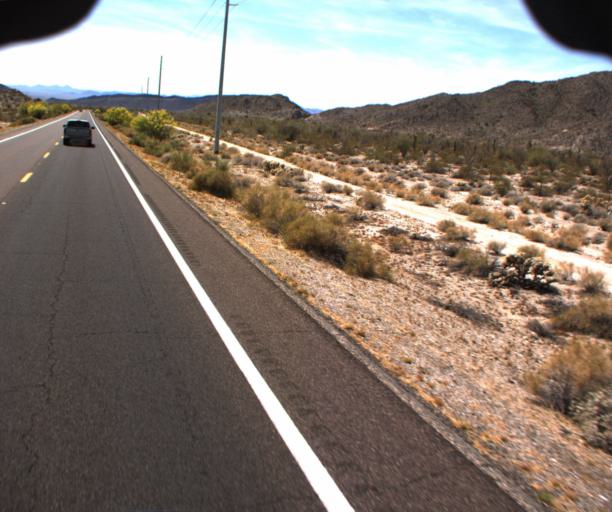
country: US
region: Arizona
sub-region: La Paz County
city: Salome
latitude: 33.7354
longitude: -113.6778
